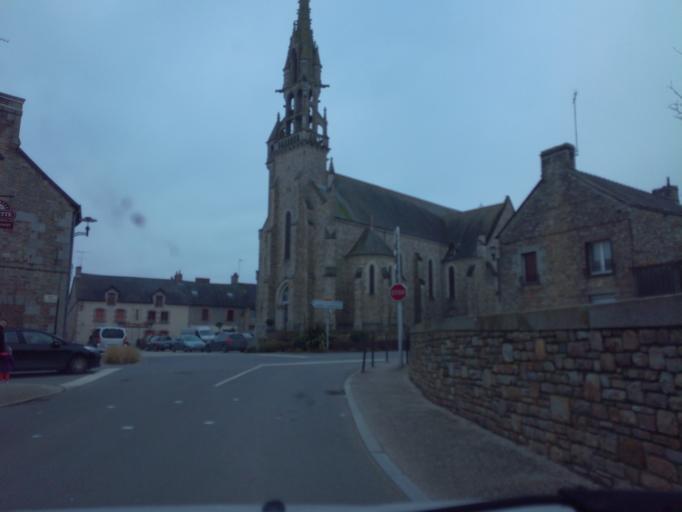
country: FR
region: Brittany
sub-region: Departement d'Ille-et-Vilaine
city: Gosne
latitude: 48.2463
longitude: -1.4628
